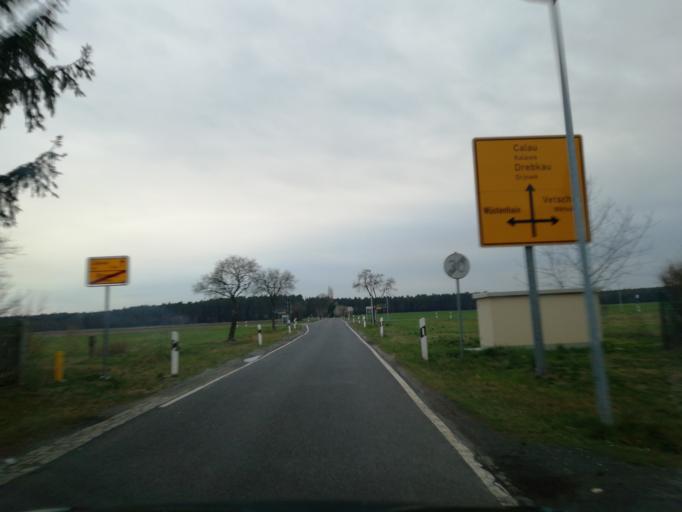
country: DE
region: Brandenburg
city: Vetschau
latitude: 51.7338
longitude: 14.1096
